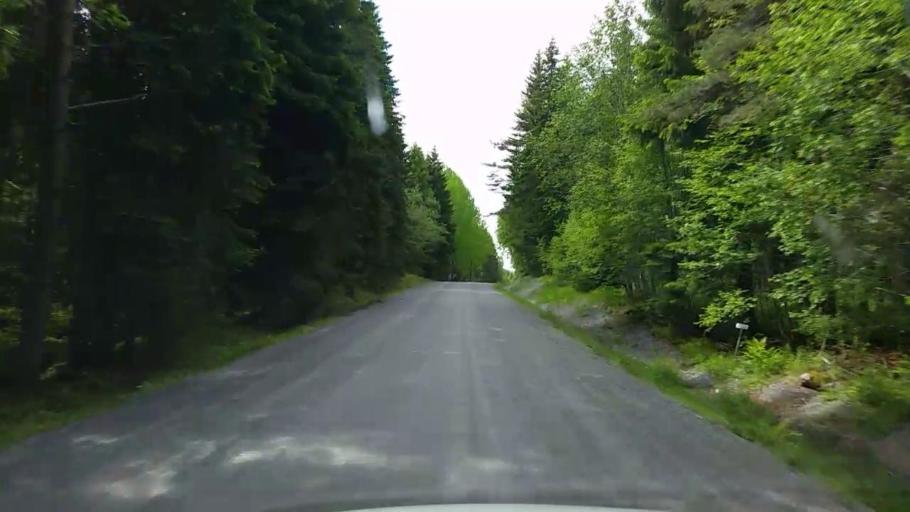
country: SE
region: Gaevleborg
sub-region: Bollnas Kommun
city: Vittsjo
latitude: 61.0920
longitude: 16.2320
